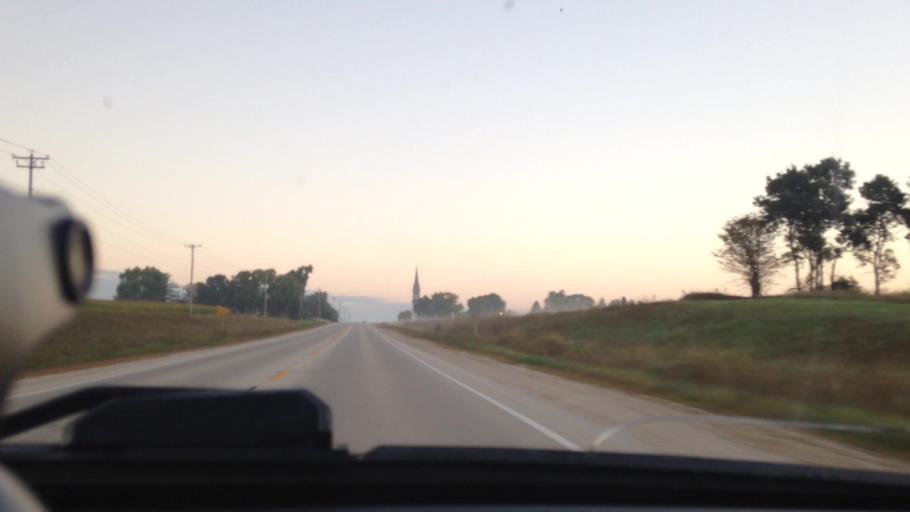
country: US
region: Wisconsin
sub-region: Dodge County
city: Theresa
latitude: 43.5472
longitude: -88.4425
